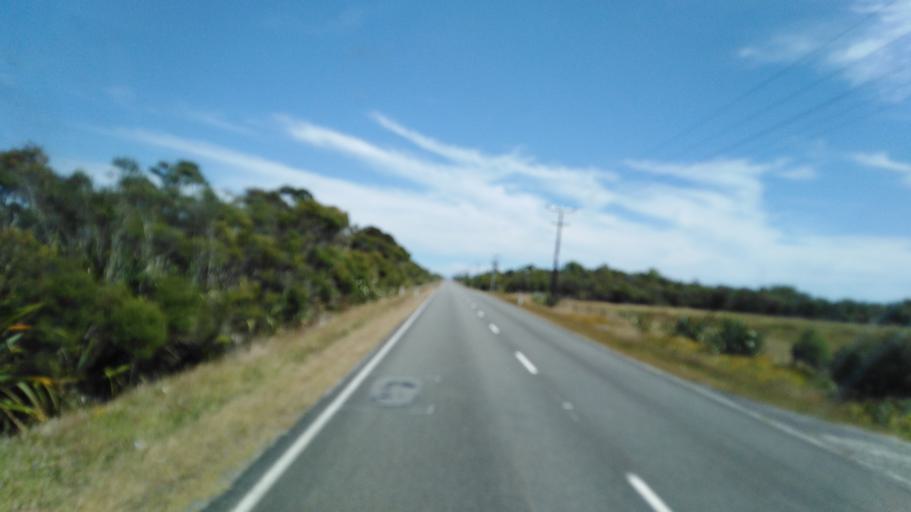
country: NZ
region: West Coast
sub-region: Buller District
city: Westport
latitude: -41.7456
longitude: 171.6850
